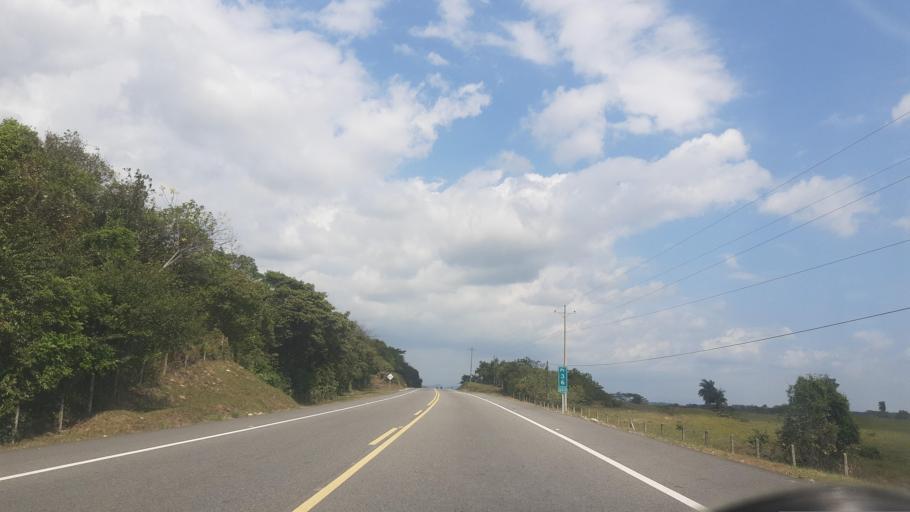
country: CO
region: Casanare
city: Tauramena
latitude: 4.9037
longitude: -72.6761
